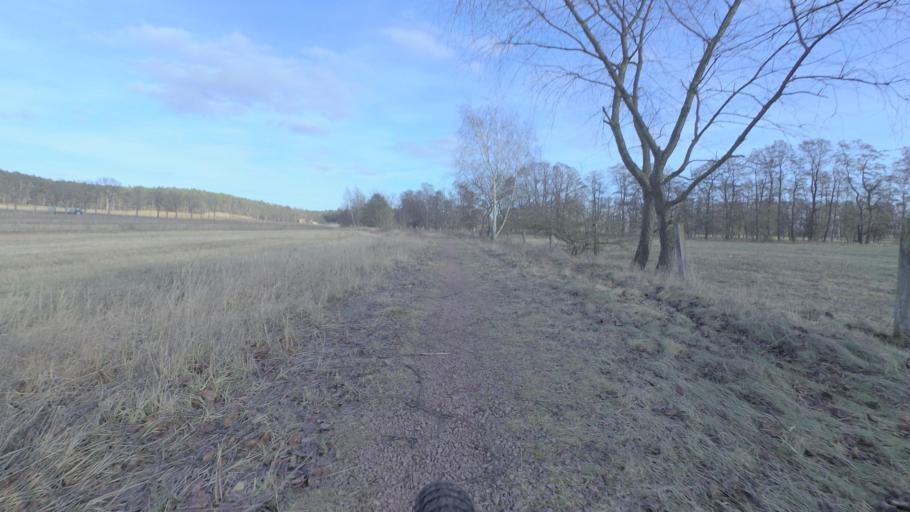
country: DE
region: Brandenburg
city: Ludwigsfelde
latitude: 52.2484
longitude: 13.2759
